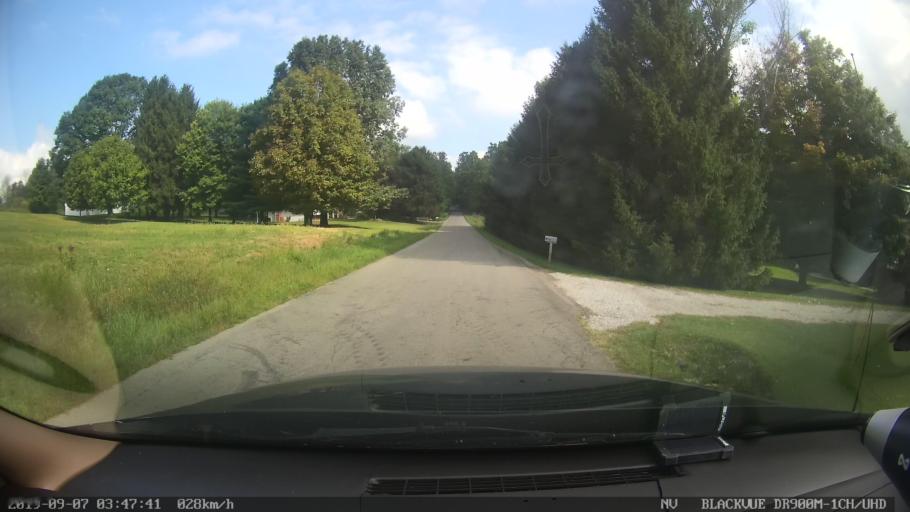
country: US
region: Ohio
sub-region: Licking County
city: Granville
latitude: 40.1425
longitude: -82.5434
